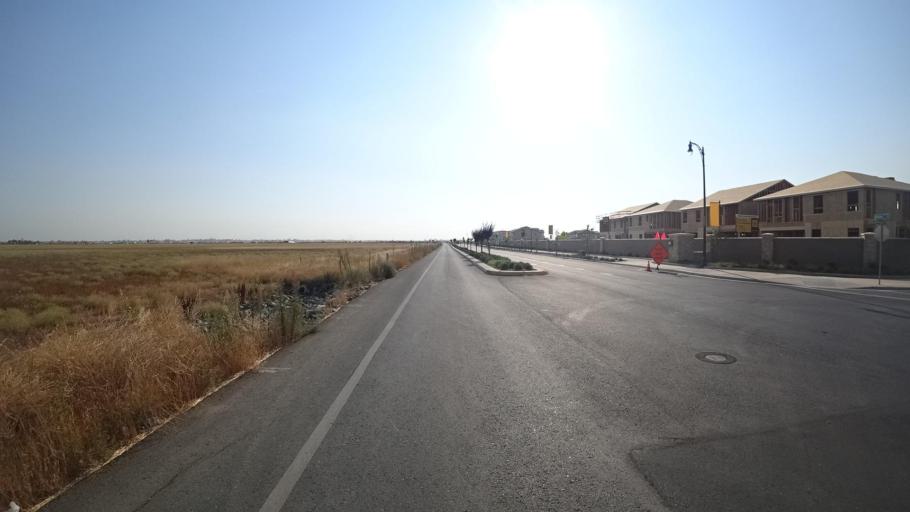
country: US
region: California
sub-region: Sacramento County
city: Elk Grove
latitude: 38.3797
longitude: -121.4042
